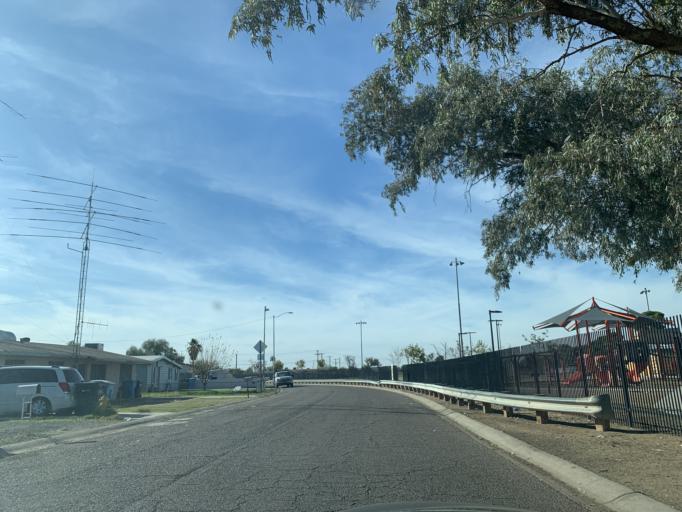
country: US
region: Arizona
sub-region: Maricopa County
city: Laveen
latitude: 33.3986
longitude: -112.1358
